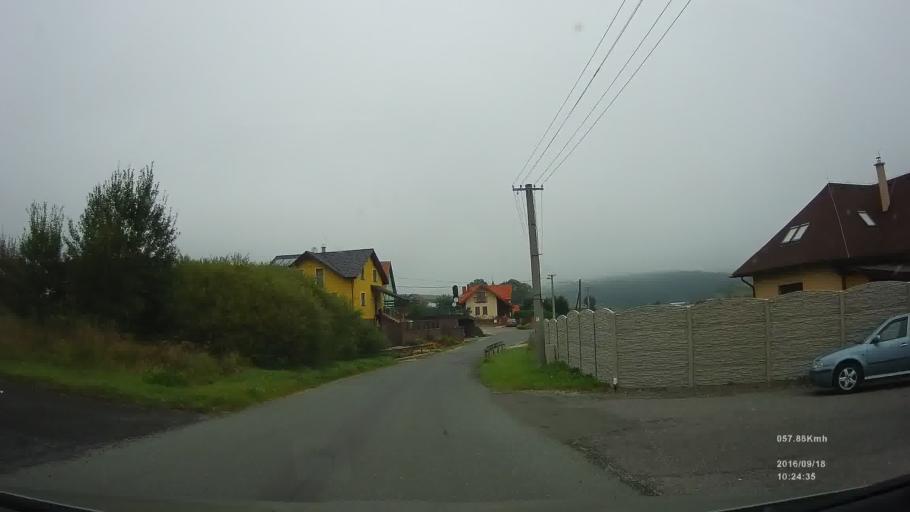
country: SK
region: Kosicky
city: Spisska Nova Ves
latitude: 48.9463
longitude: 20.6177
